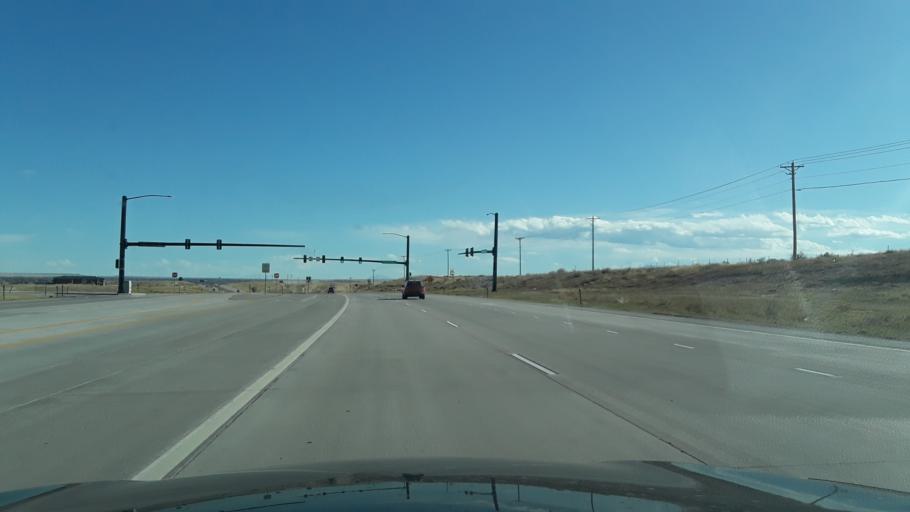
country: US
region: Colorado
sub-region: Pueblo County
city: Pueblo West
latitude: 38.3088
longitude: -104.6634
